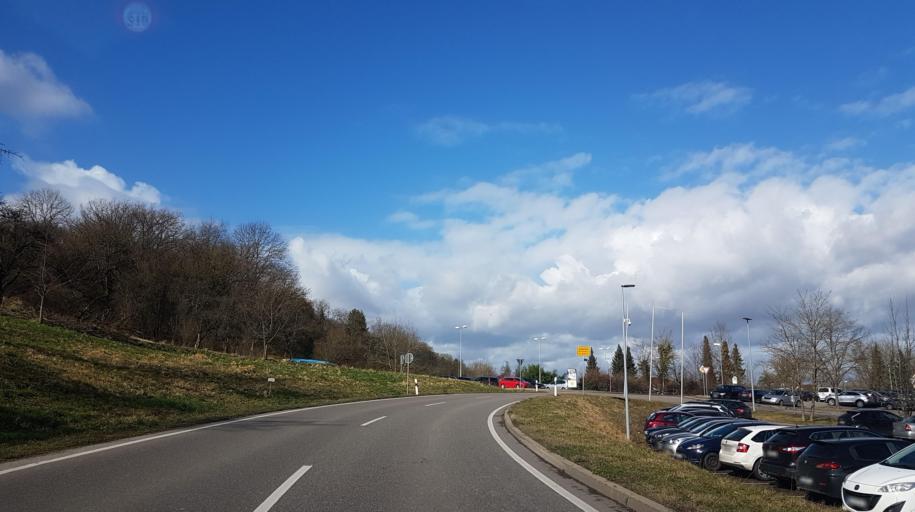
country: DE
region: Baden-Wuerttemberg
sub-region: Regierungsbezirk Stuttgart
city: Neuenstadt am Kocher
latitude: 49.2404
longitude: 9.3064
